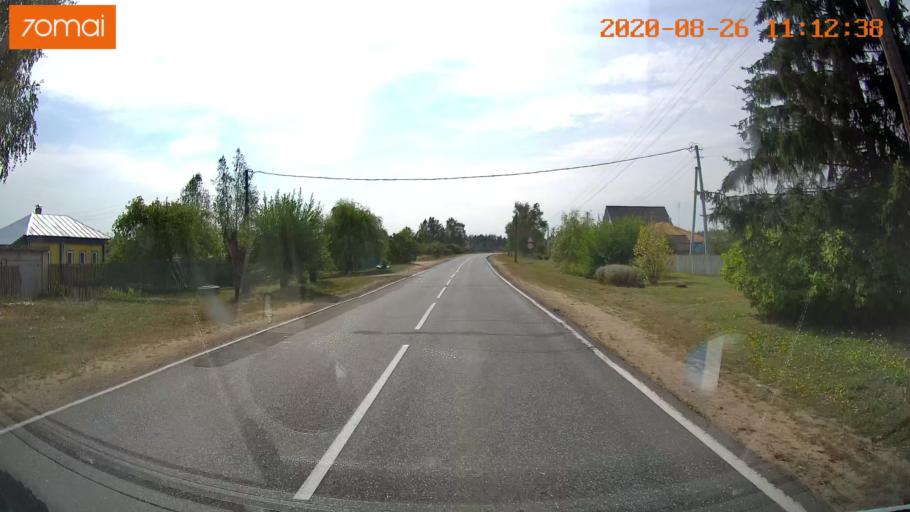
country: RU
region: Rjazan
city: Izhevskoye
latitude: 54.4682
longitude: 41.1248
